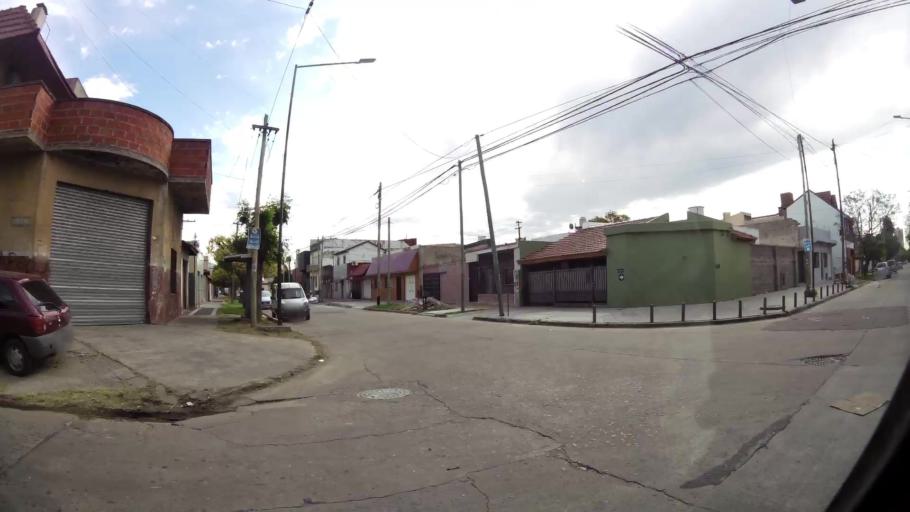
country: AR
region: Buenos Aires
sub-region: Partido de Lanus
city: Lanus
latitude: -34.6958
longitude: -58.3821
